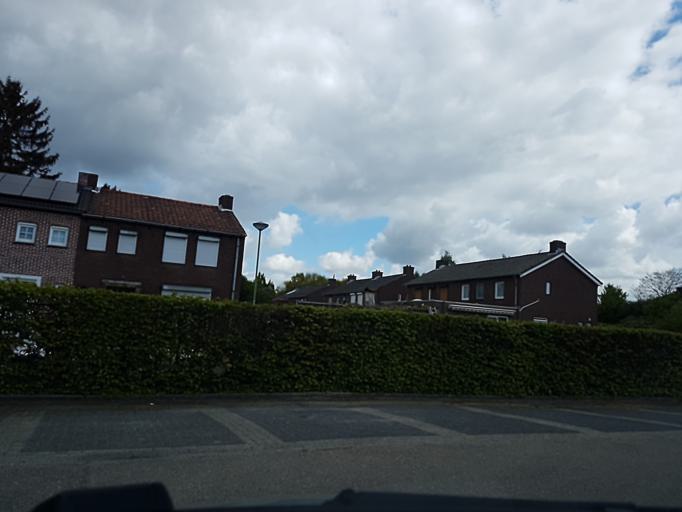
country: NL
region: Limburg
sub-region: Gemeente Stein
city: Urmond
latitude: 50.9894
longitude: 5.7810
